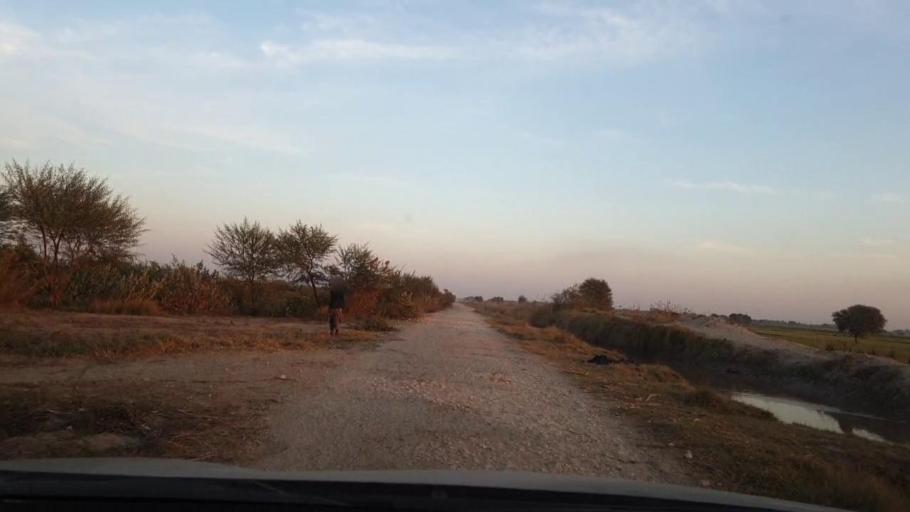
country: PK
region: Sindh
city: Tando Allahyar
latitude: 25.5833
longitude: 68.7234
